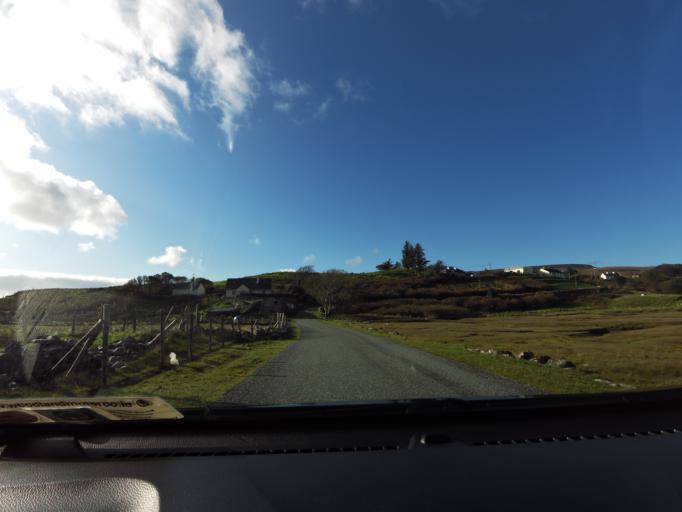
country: IE
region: Connaught
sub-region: Maigh Eo
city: Westport
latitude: 53.8984
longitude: -9.7872
